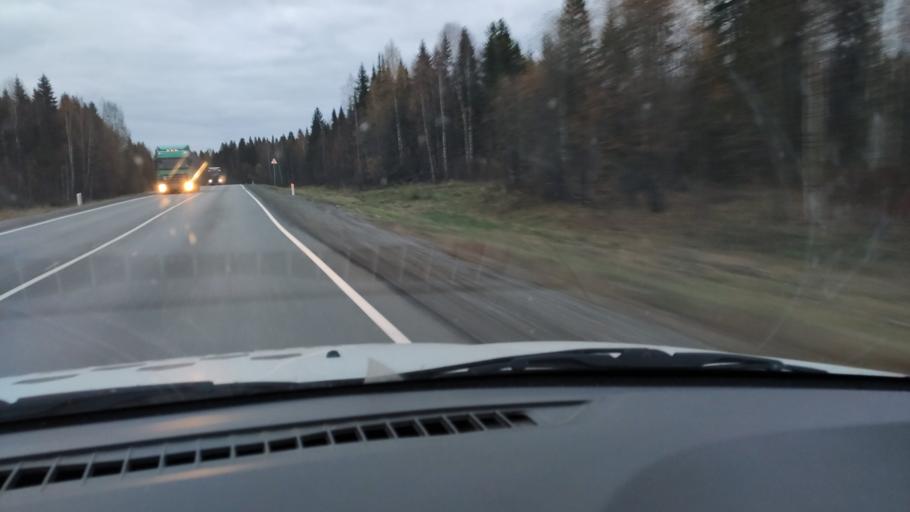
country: RU
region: Kirov
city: Kostino
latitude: 58.7939
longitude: 52.8718
